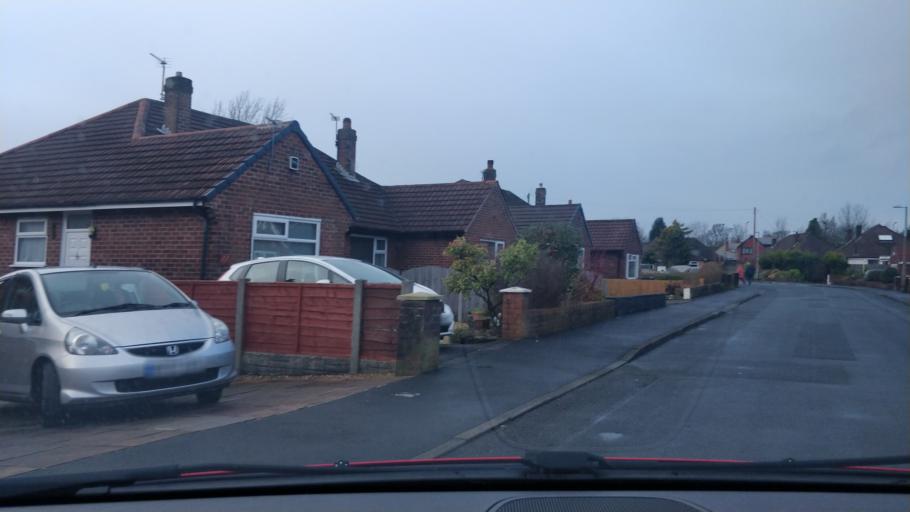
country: GB
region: England
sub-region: Lancashire
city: Preston
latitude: 53.7424
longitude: -2.7424
